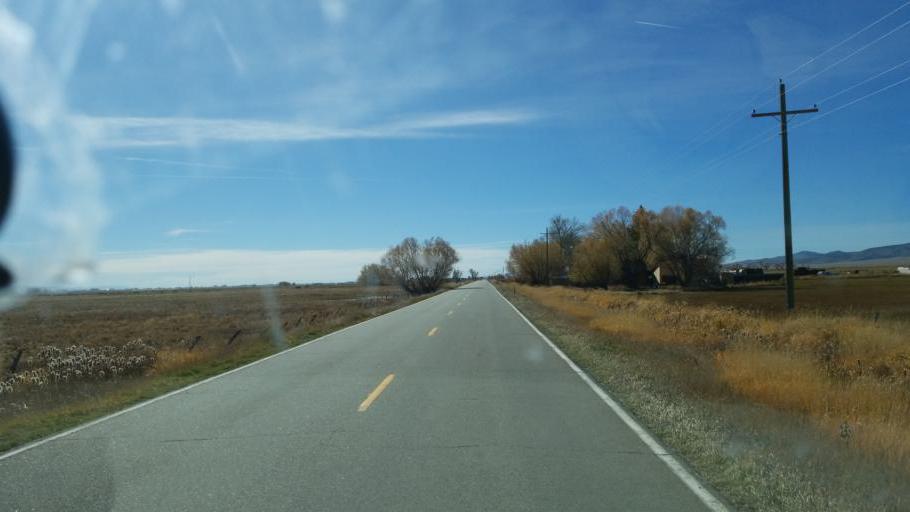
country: US
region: Colorado
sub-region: Rio Grande County
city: Monte Vista
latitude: 37.5279
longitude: -106.1493
